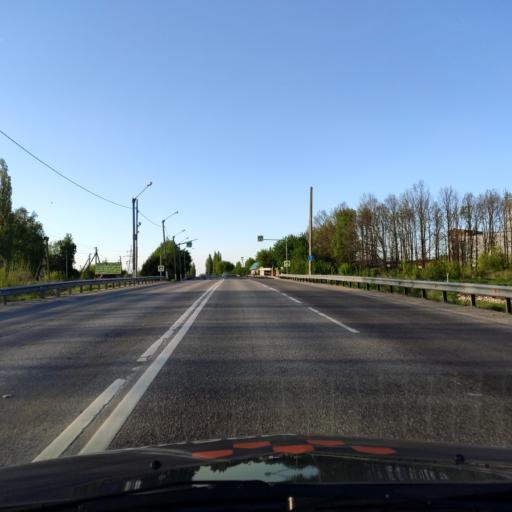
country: RU
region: Lipetsk
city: Yelets
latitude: 52.6135
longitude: 38.4616
